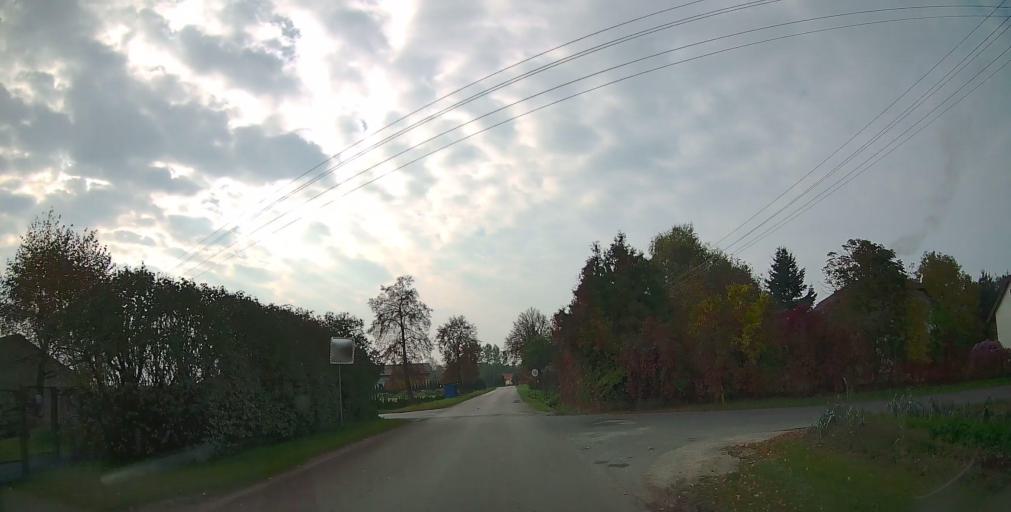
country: PL
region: Masovian Voivodeship
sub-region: Powiat grojecki
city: Mogielnica
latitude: 51.6680
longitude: 20.7114
